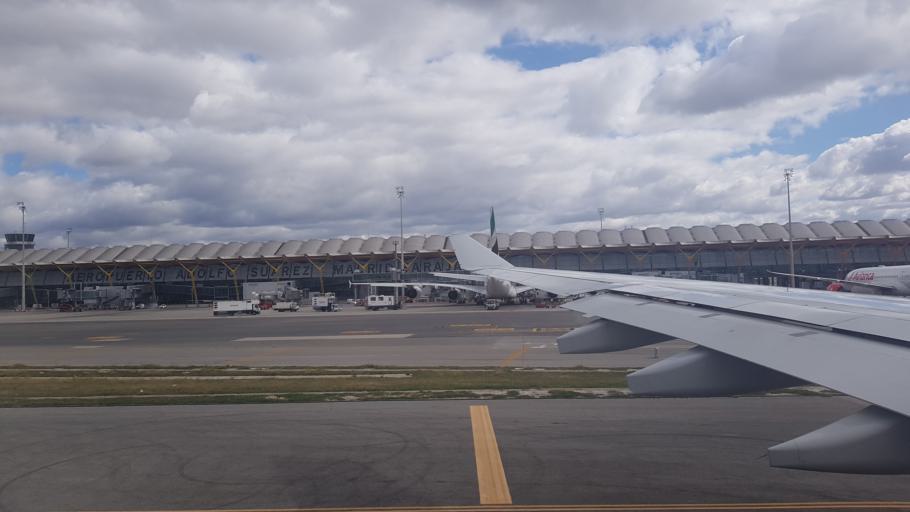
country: ES
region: Madrid
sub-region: Provincia de Madrid
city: Barajas de Madrid
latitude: 40.4935
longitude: -3.5711
